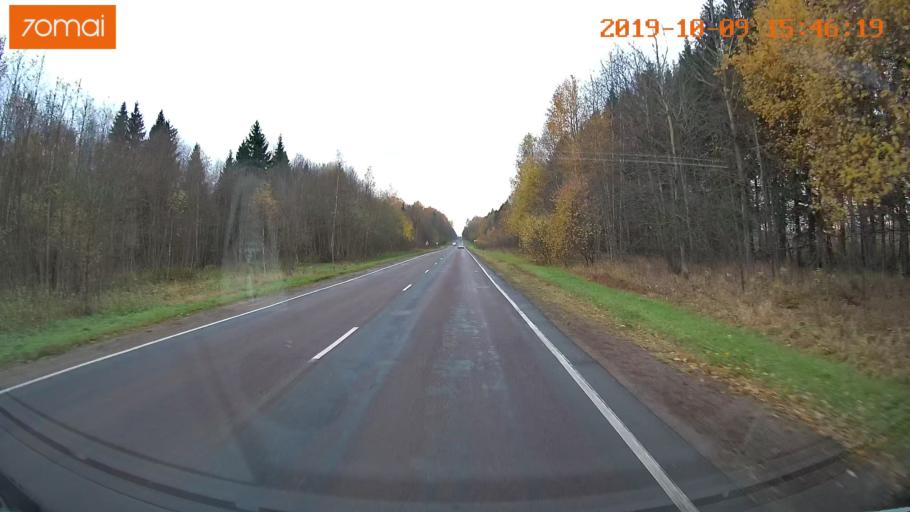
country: RU
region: Kostroma
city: Oktyabr'skiy
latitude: 57.8258
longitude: 41.0462
